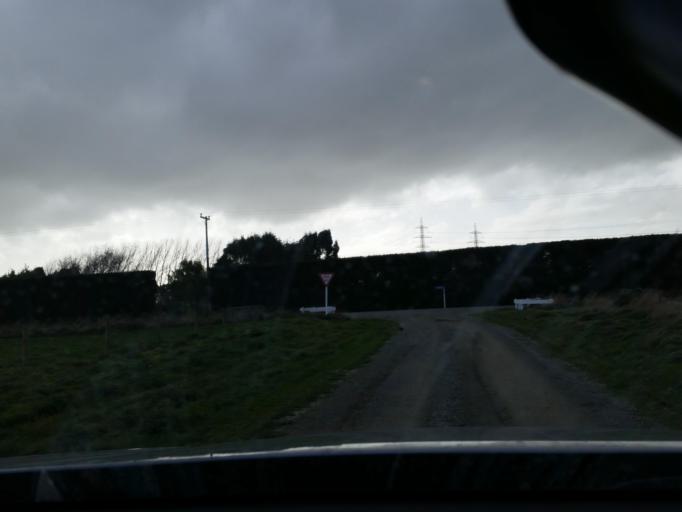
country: NZ
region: Southland
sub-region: Invercargill City
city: Invercargill
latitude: -46.3229
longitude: 168.3754
